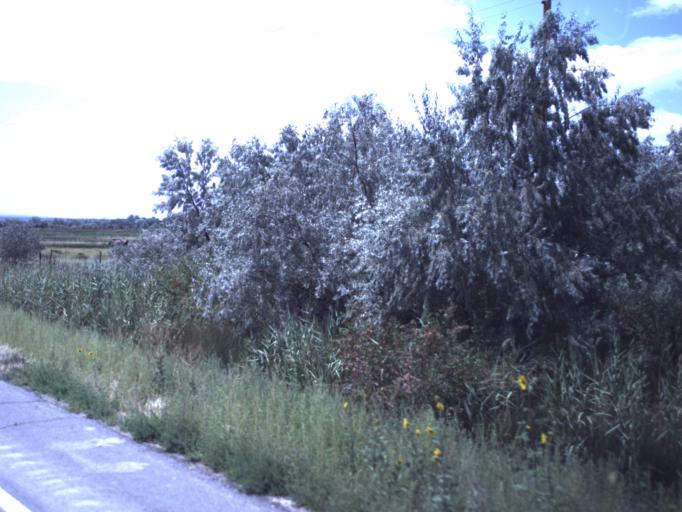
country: US
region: Utah
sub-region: Duchesne County
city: Roosevelt
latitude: 40.1625
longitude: -110.1610
